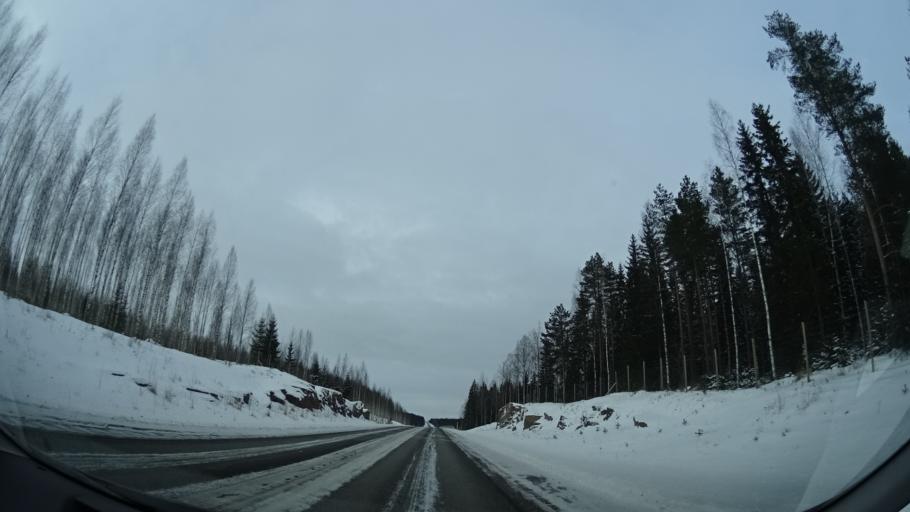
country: FI
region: Uusimaa
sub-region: Helsinki
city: Kaerkoelae
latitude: 60.6201
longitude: 24.0036
